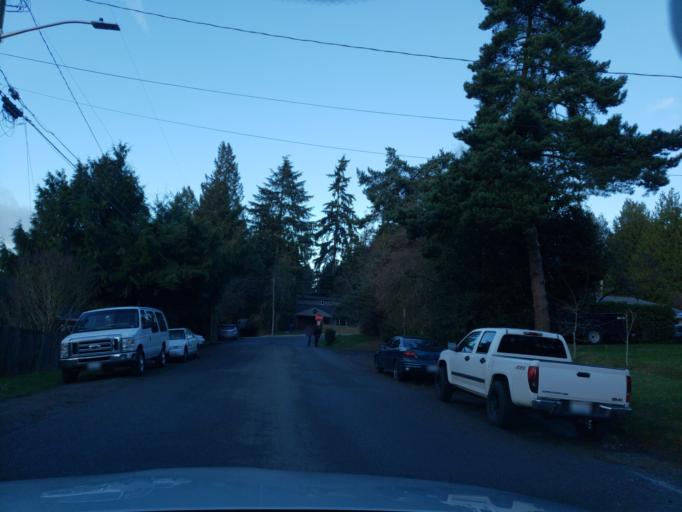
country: US
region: Washington
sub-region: King County
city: Shoreline
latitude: 47.7672
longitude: -122.3423
